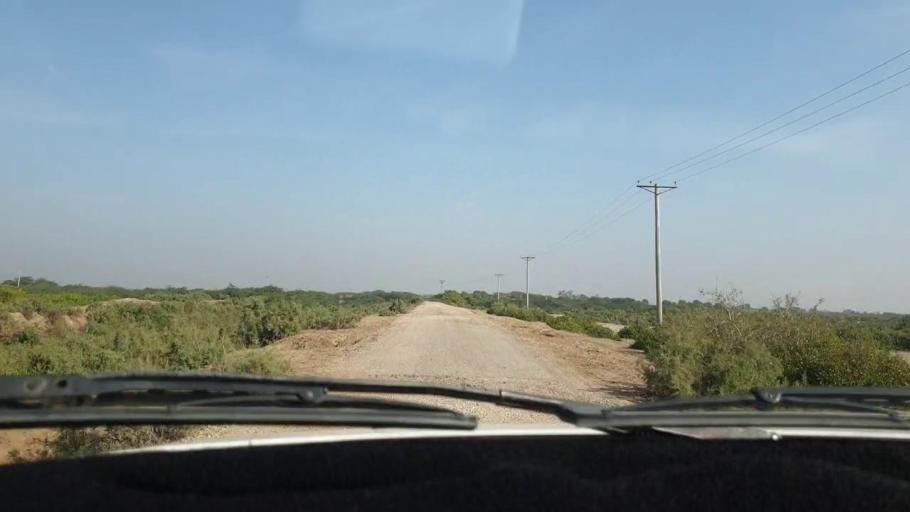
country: PK
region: Sindh
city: Bulri
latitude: 24.9751
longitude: 68.4585
